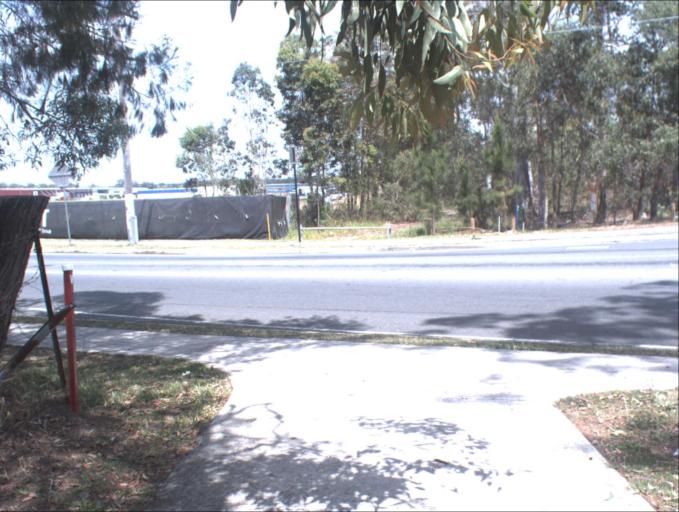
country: AU
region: Queensland
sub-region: Logan
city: Logan City
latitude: -27.6438
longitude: 153.1003
